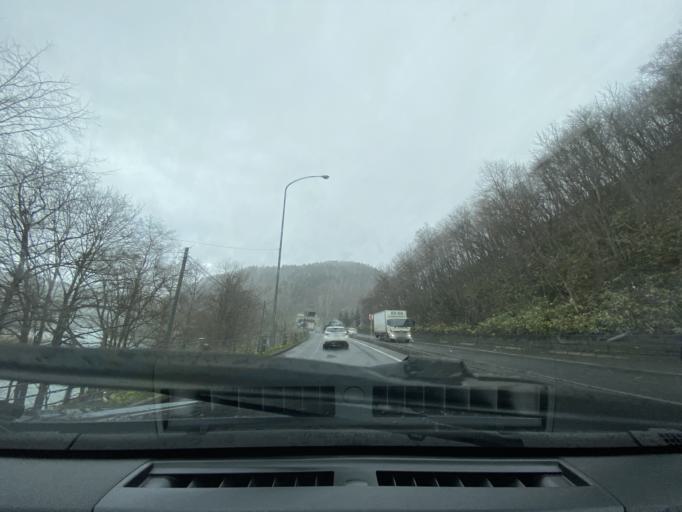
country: JP
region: Hokkaido
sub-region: Asahikawa-shi
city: Asahikawa
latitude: 43.7375
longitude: 142.2418
